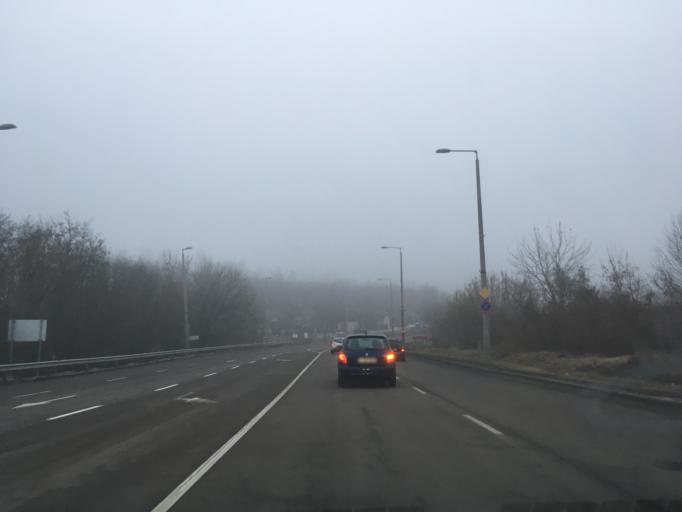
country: HU
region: Heves
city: Eger
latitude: 47.8703
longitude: 20.3824
